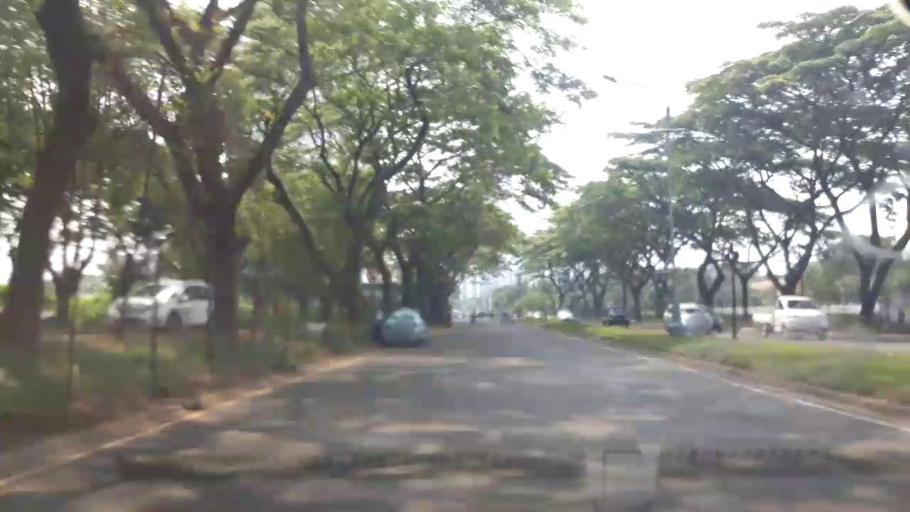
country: ID
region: Banten
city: Tangerang
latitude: -6.2262
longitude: 106.5993
